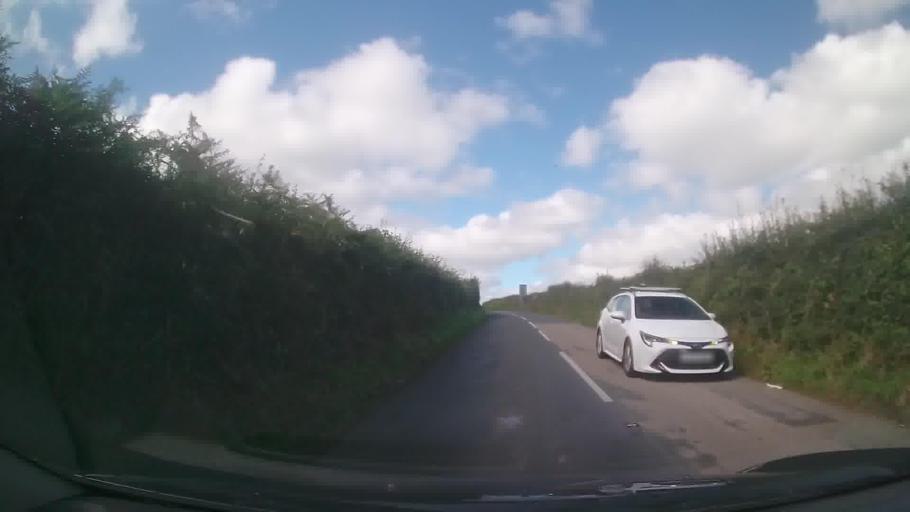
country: GB
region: Wales
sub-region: Pembrokeshire
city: Penally
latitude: 51.6576
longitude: -4.7434
